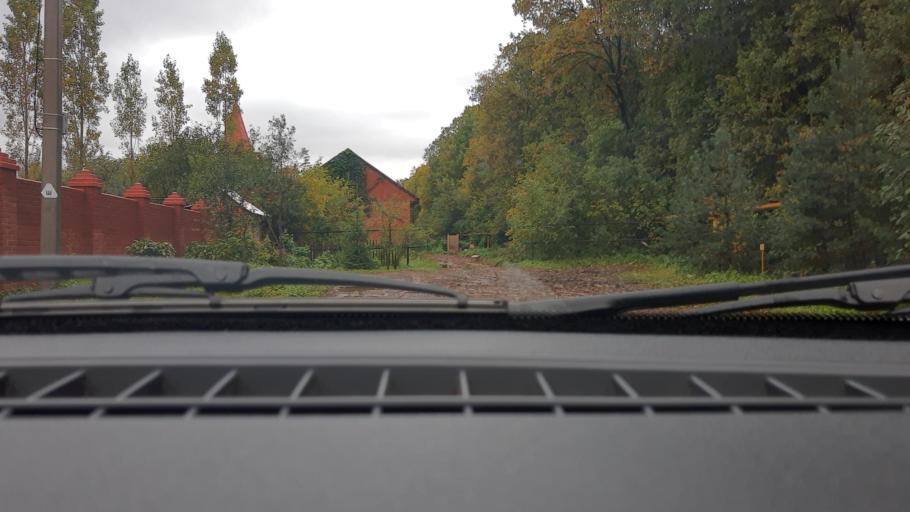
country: RU
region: Bashkortostan
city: Mikhaylovka
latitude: 54.7883
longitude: 55.8950
